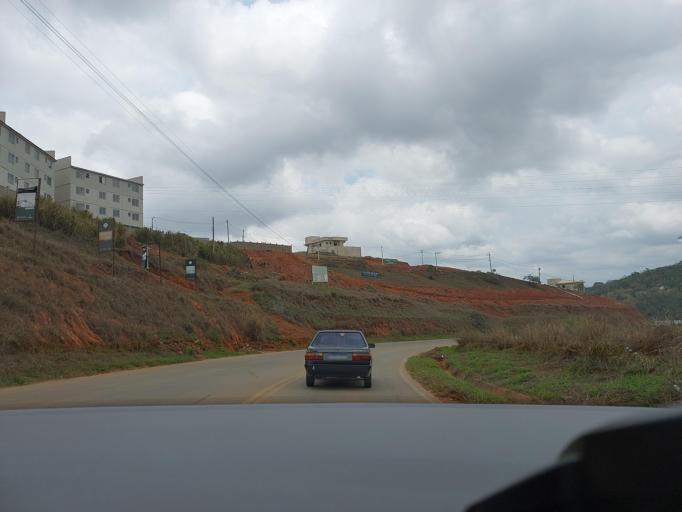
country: BR
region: Minas Gerais
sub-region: Ponte Nova
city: Ponte Nova
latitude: -20.3962
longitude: -42.8725
